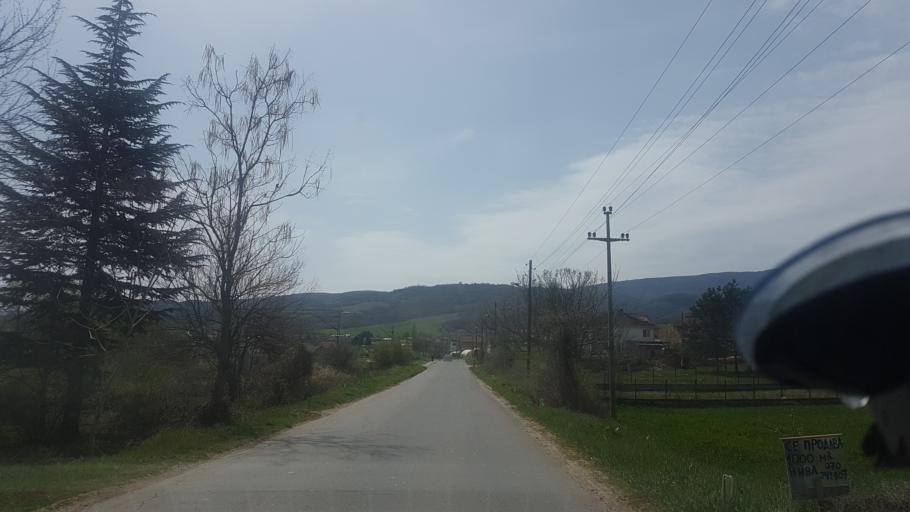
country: MK
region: Zelenikovo
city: Zelenikovo
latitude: 41.8892
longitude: 21.5876
